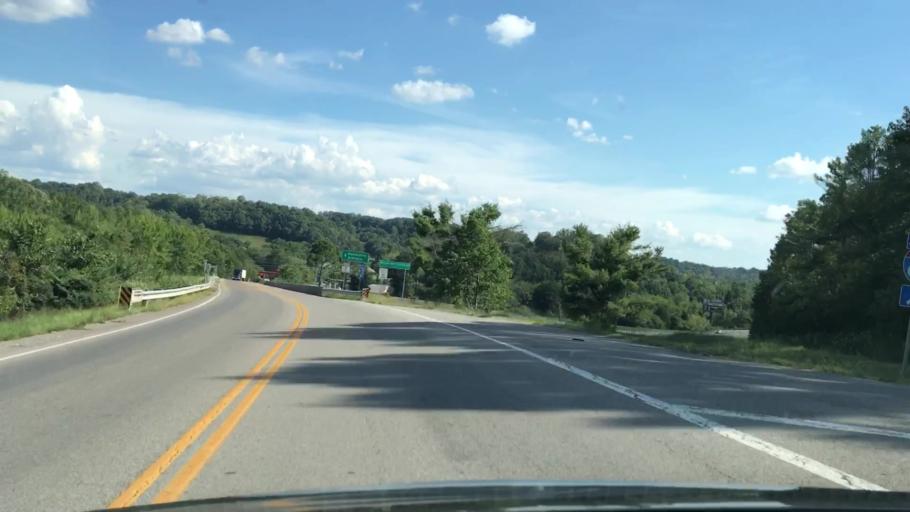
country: US
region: Alabama
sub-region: Limestone County
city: Ardmore
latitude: 35.0142
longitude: -86.8804
